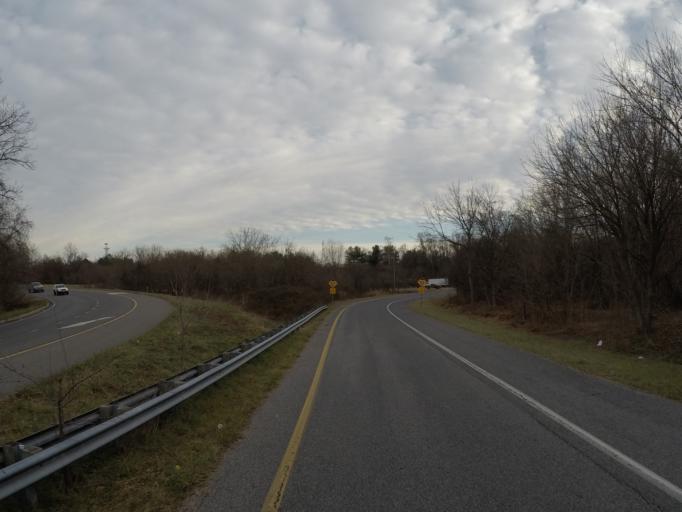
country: US
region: Maryland
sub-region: Howard County
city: Riverside
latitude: 39.1721
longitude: -76.8531
